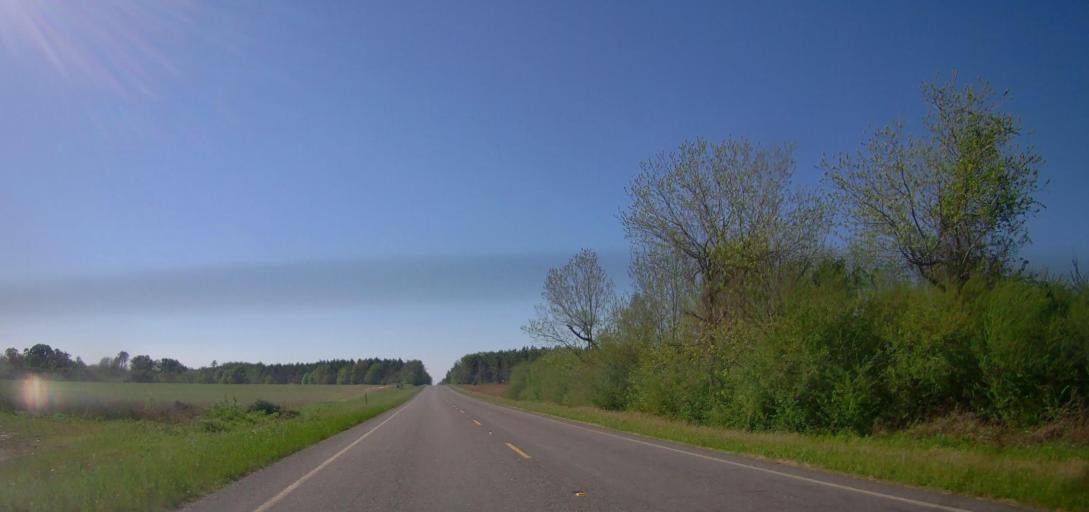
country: US
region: Georgia
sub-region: Wilcox County
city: Rochelle
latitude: 31.9919
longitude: -83.4690
